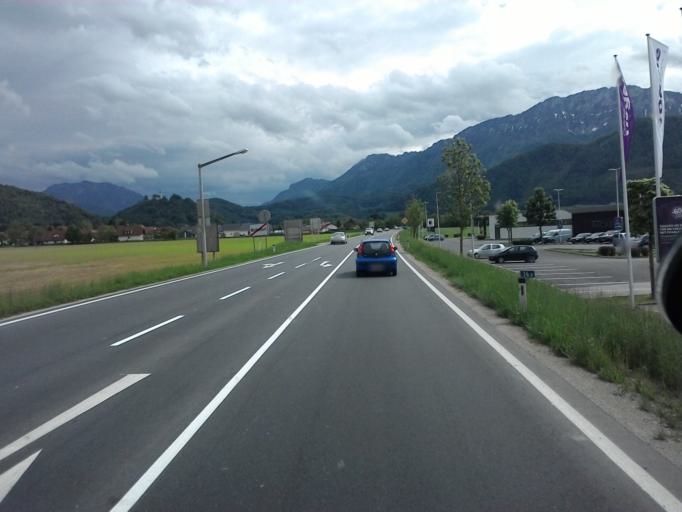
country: AT
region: Upper Austria
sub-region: Politischer Bezirk Kirchdorf an der Krems
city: Micheldorf in Oberoesterreich
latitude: 47.8911
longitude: 14.1285
